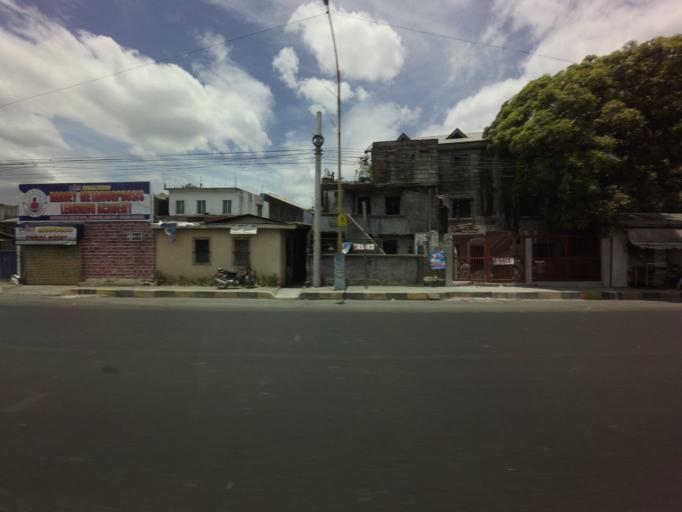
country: PH
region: Metro Manila
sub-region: Marikina
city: Calumpang
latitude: 14.5957
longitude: 121.0918
